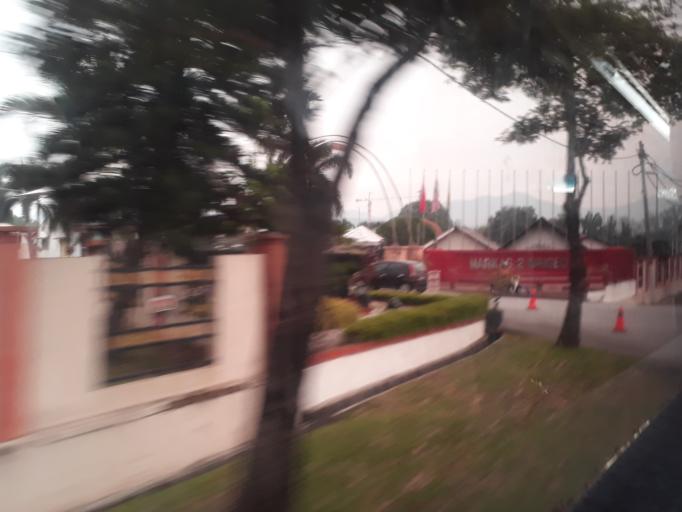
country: MY
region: Perak
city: Ipoh
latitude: 4.5995
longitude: 101.1048
